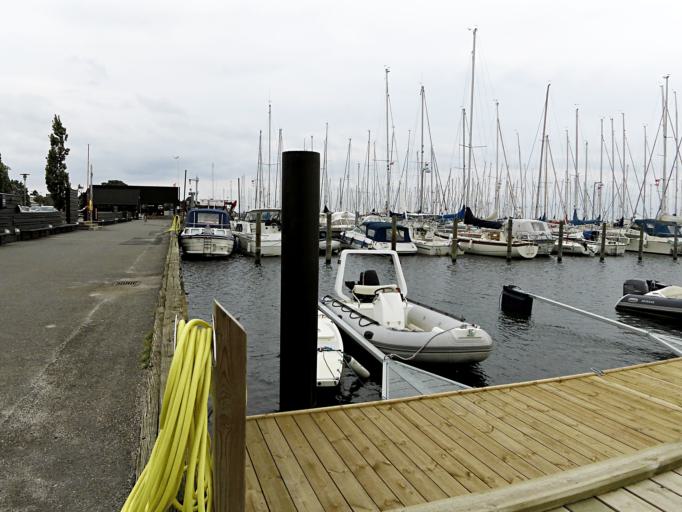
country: DK
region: Capital Region
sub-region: Rudersdal Kommune
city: Trorod
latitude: 55.8484
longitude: 12.5719
